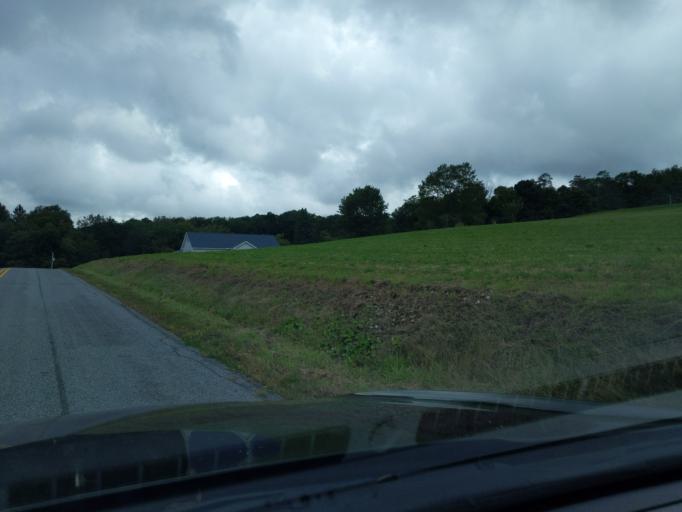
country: US
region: Pennsylvania
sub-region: Cambria County
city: Portage
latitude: 40.3198
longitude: -78.5725
